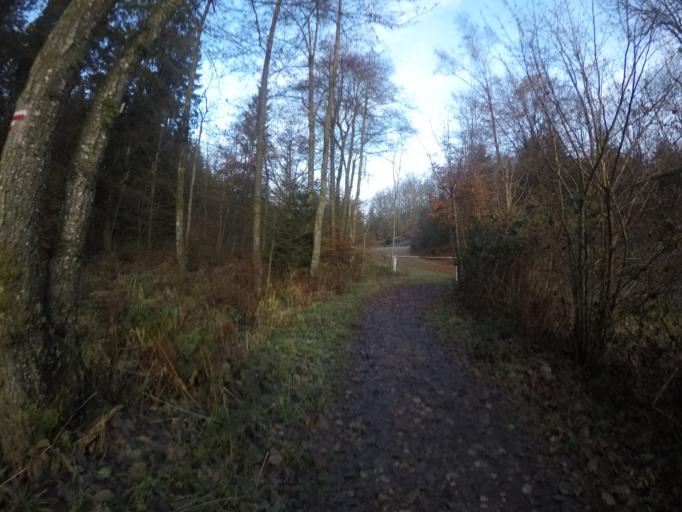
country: BE
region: Wallonia
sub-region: Province du Luxembourg
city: Habay-la-Vieille
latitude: 49.7433
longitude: 5.6722
